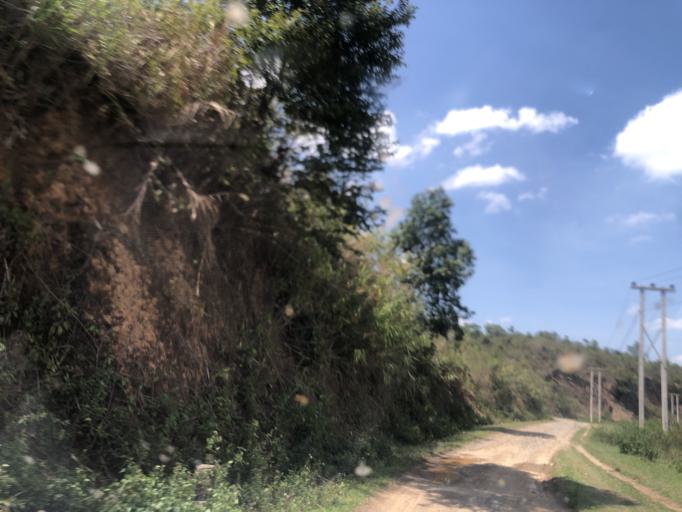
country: LA
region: Phongsali
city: Phongsali
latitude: 21.4100
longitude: 102.2398
